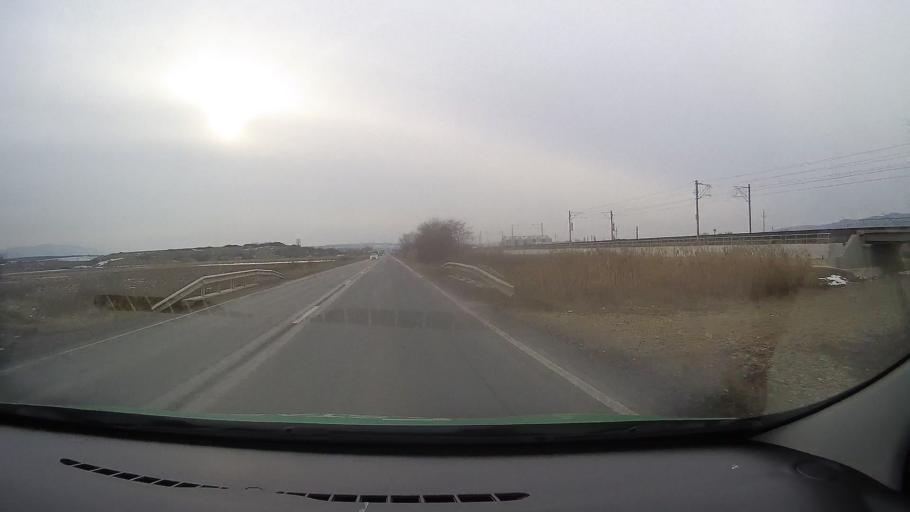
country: RO
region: Hunedoara
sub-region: Municipiul Orastie
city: Orastie
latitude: 45.8729
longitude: 23.2332
